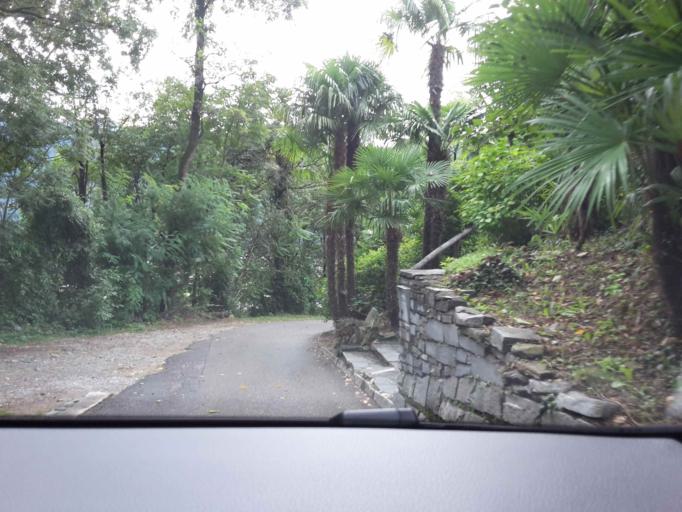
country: CH
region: Ticino
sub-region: Bellinzona District
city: Sementina
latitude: 46.1798
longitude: 8.9718
